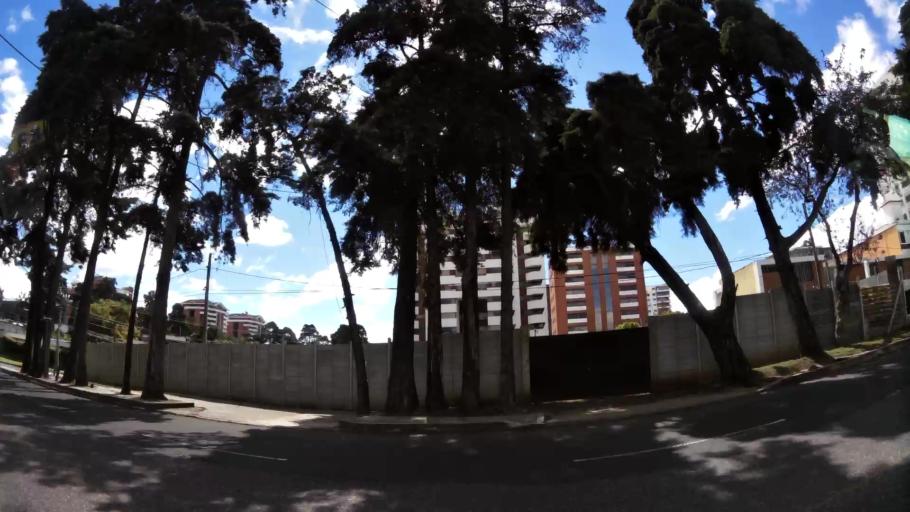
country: GT
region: Guatemala
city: Santa Catarina Pinula
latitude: 14.5853
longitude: -90.5175
